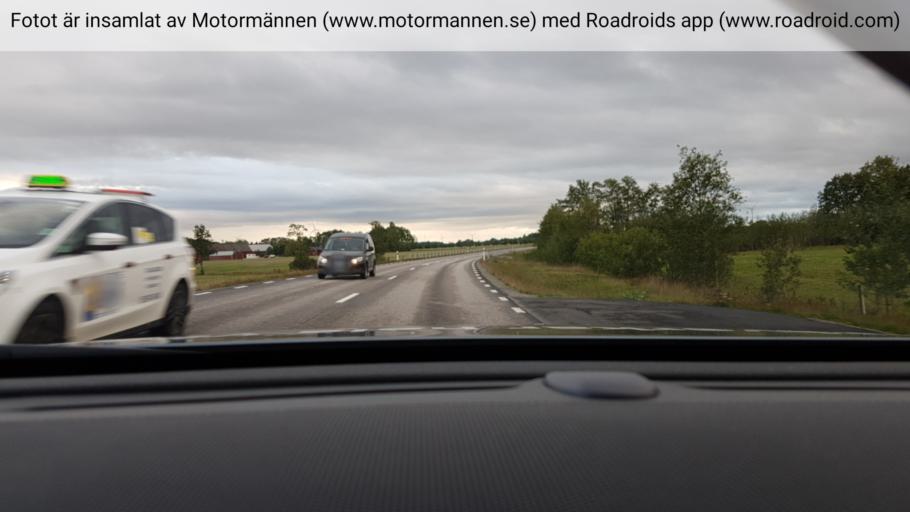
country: SE
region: Vaestra Goetaland
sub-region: Melleruds Kommun
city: Mellerud
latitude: 58.6478
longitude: 12.4152
